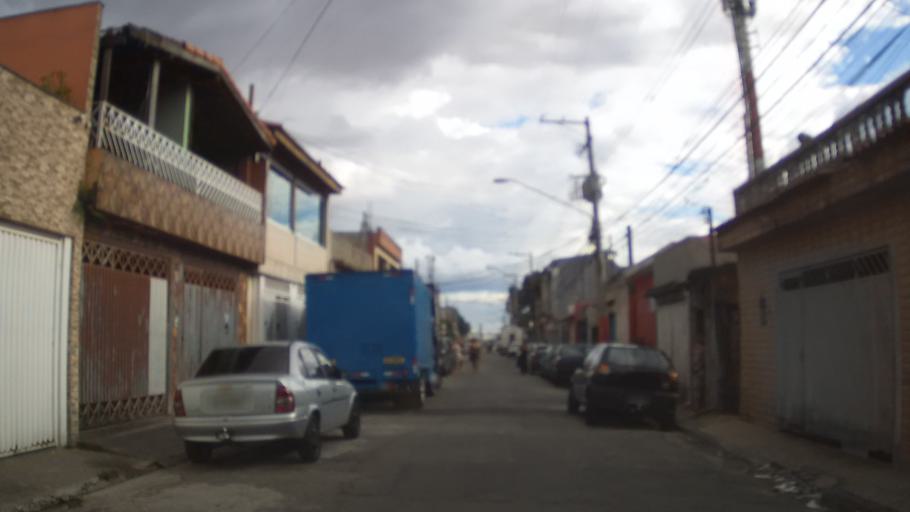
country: BR
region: Sao Paulo
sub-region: Guarulhos
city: Guarulhos
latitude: -23.4790
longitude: -46.5569
